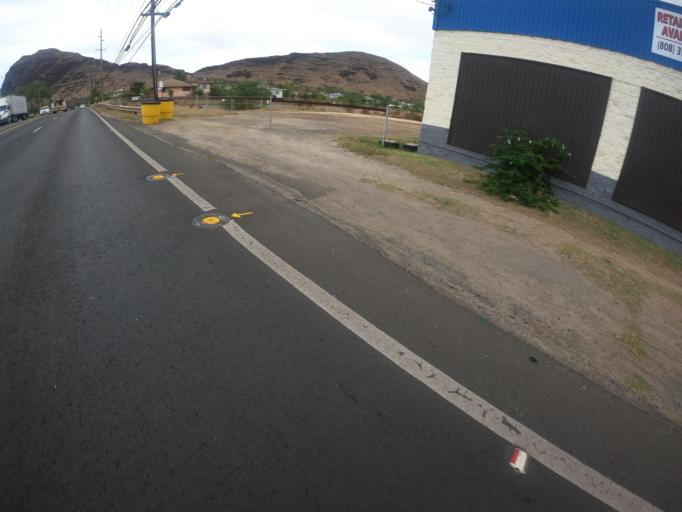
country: US
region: Hawaii
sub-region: Honolulu County
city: Nanakuli
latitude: 21.3921
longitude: -158.1569
